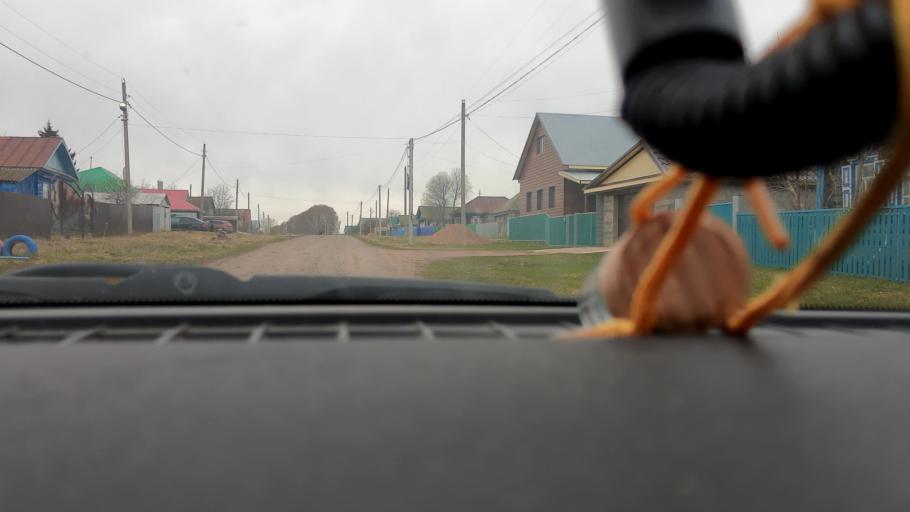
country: RU
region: Bashkortostan
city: Asanovo
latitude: 54.8183
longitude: 55.5637
